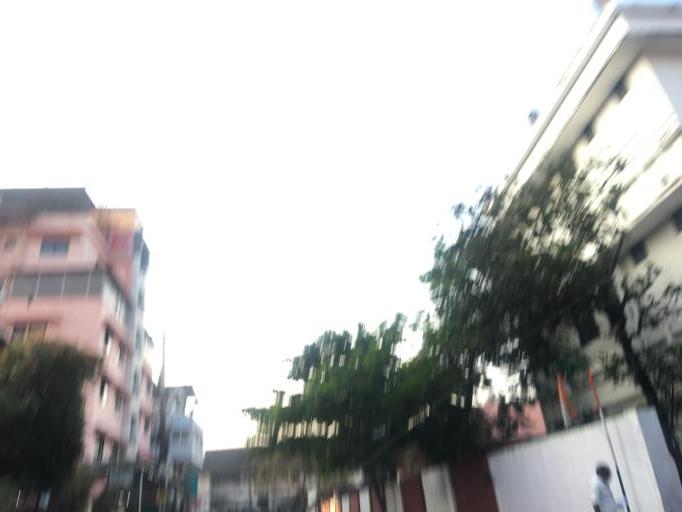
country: IN
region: Kerala
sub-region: Ernakulam
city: Cochin
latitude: 9.9730
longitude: 76.2812
